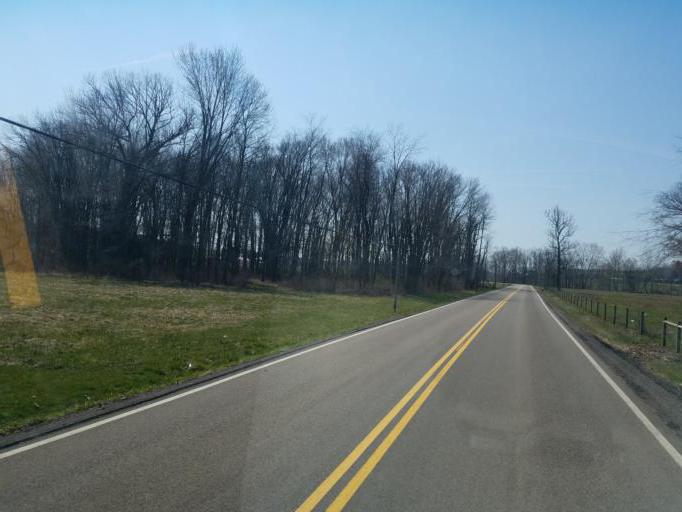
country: US
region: Ohio
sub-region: Knox County
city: Danville
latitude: 40.4992
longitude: -82.2870
